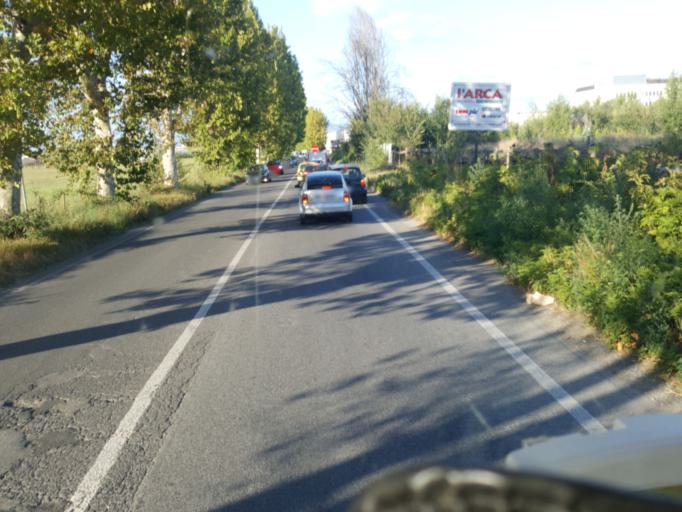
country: IT
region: Latium
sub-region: Citta metropolitana di Roma Capitale
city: Girardi-Bellavista-Terrazze
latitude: 42.1095
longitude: 12.5842
